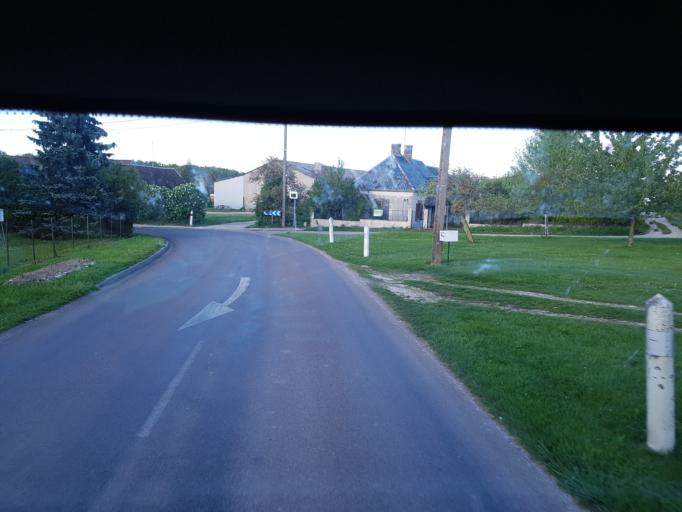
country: FR
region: Champagne-Ardenne
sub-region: Departement de l'Aube
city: Marigny-le-Chatel
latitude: 48.3460
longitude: 3.6357
